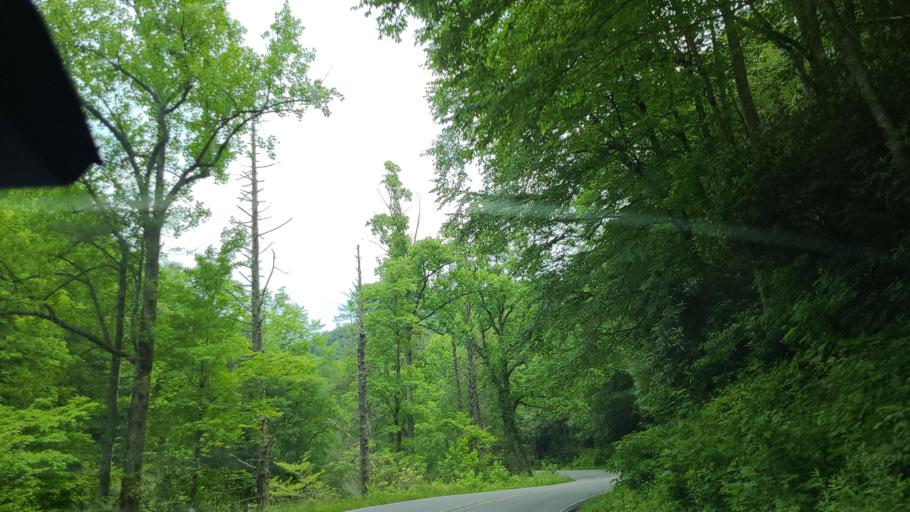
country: US
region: North Carolina
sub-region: Macon County
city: Franklin
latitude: 35.0983
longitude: -83.2626
